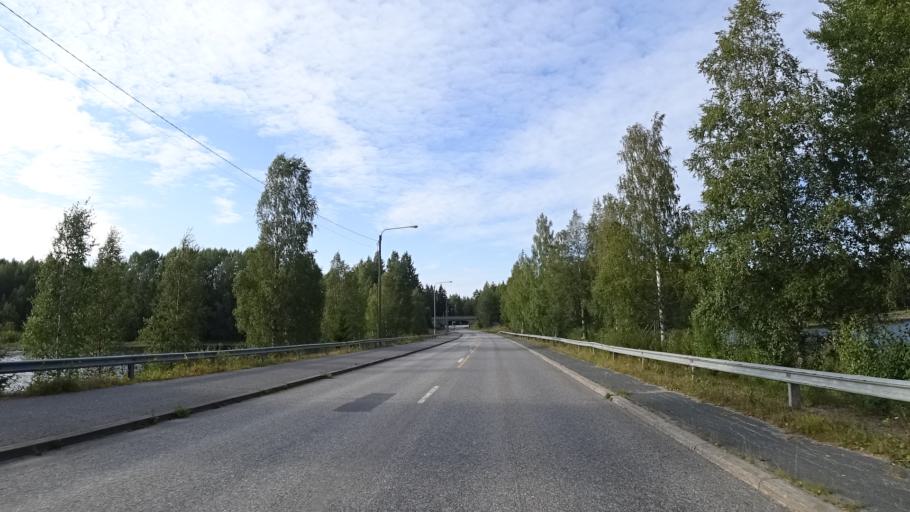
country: FI
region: North Karelia
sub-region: Joensuu
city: Eno
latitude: 62.8051
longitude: 30.1525
